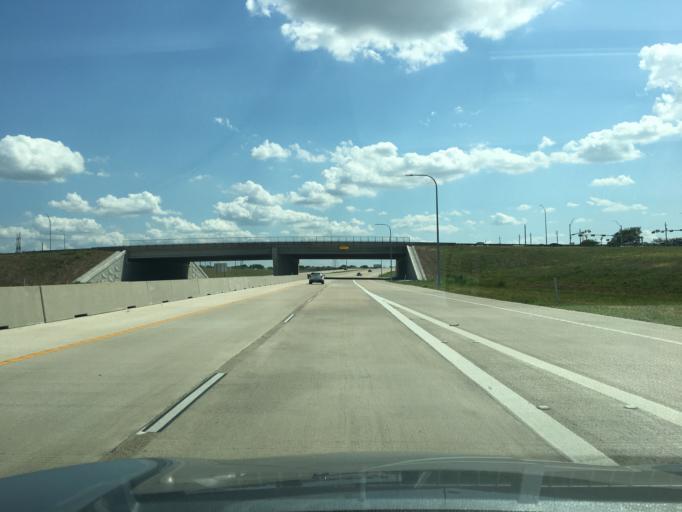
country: US
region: Texas
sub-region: Tarrant County
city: Mansfield
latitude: 32.6373
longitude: -97.0642
